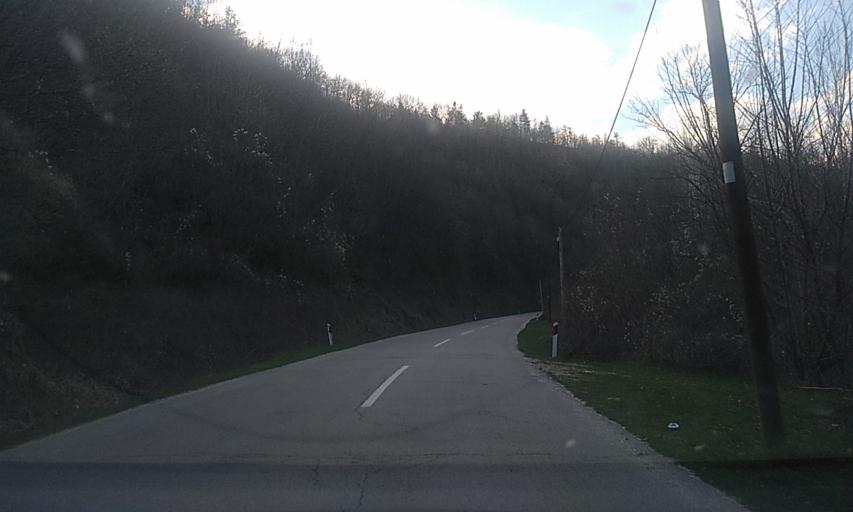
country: RS
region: Central Serbia
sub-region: Pcinjski Okrug
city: Bosilegrad
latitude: 42.4320
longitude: 22.5134
